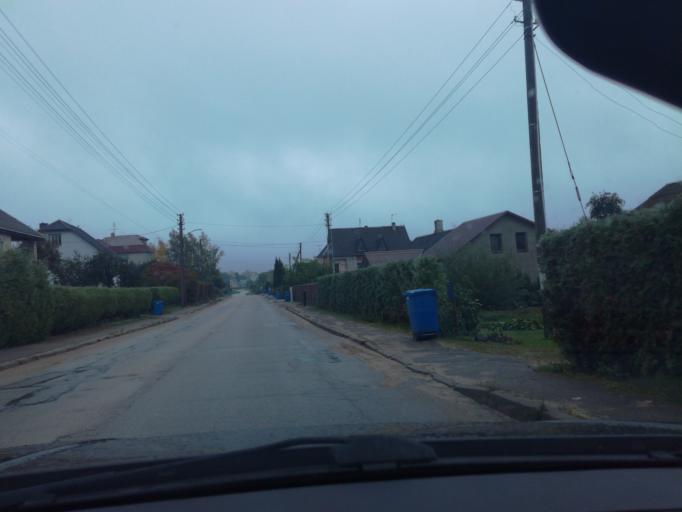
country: LT
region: Alytaus apskritis
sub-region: Alytus
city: Alytus
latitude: 54.3995
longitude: 24.0782
